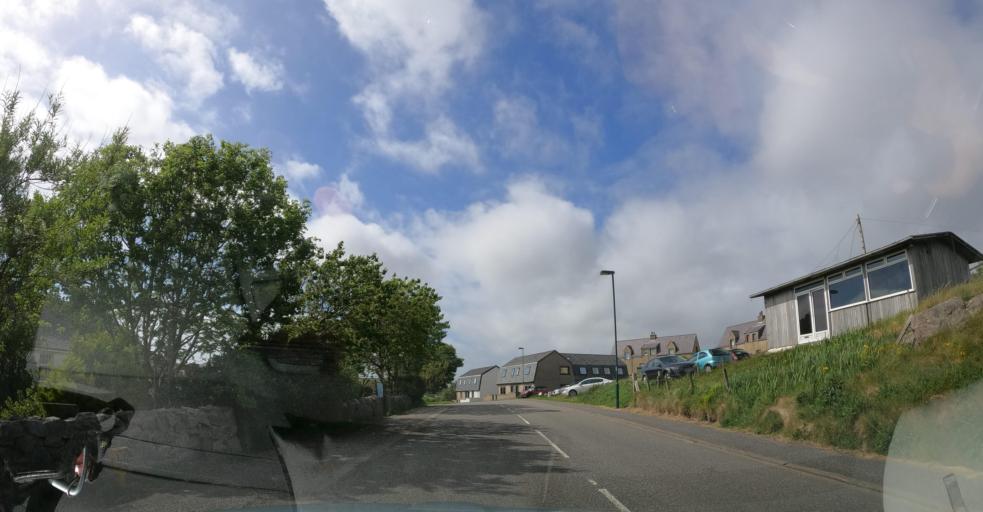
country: GB
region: Scotland
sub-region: Eilean Siar
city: Isle of South Uist
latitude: 57.1540
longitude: -7.3093
